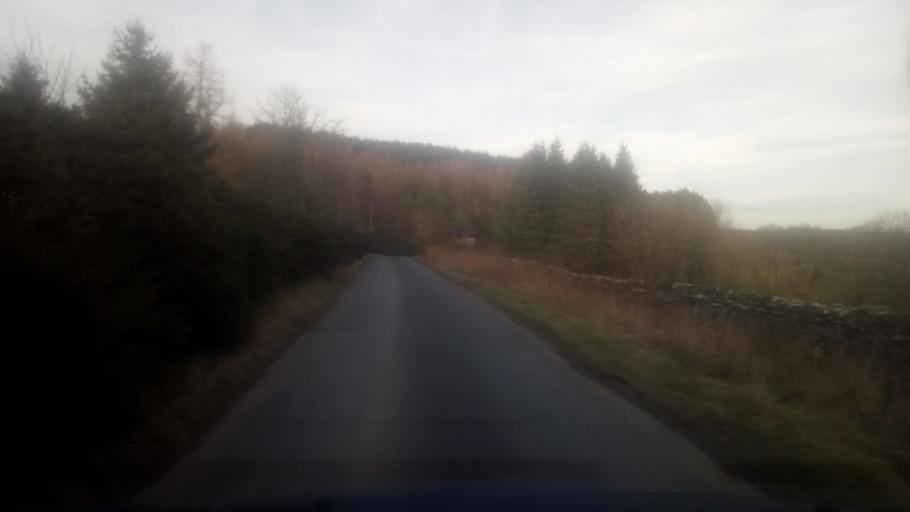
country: GB
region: Scotland
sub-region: The Scottish Borders
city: Jedburgh
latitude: 55.3941
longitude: -2.5656
